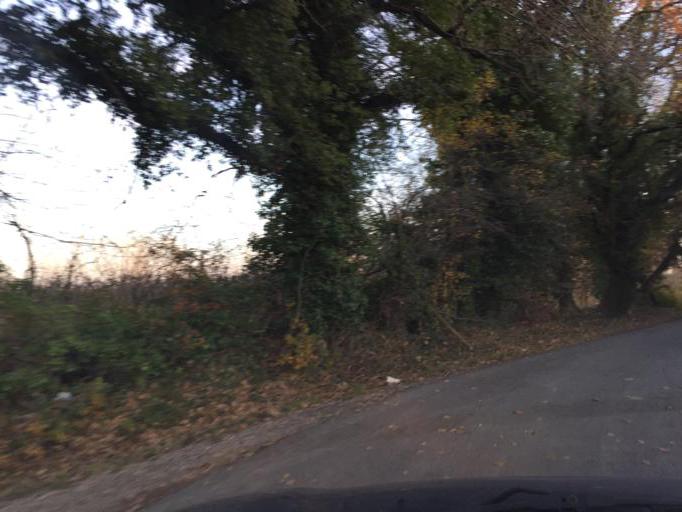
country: FR
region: Provence-Alpes-Cote d'Azur
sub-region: Departement du Vaucluse
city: Camaret-sur-Aigues
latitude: 44.1272
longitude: 4.8561
